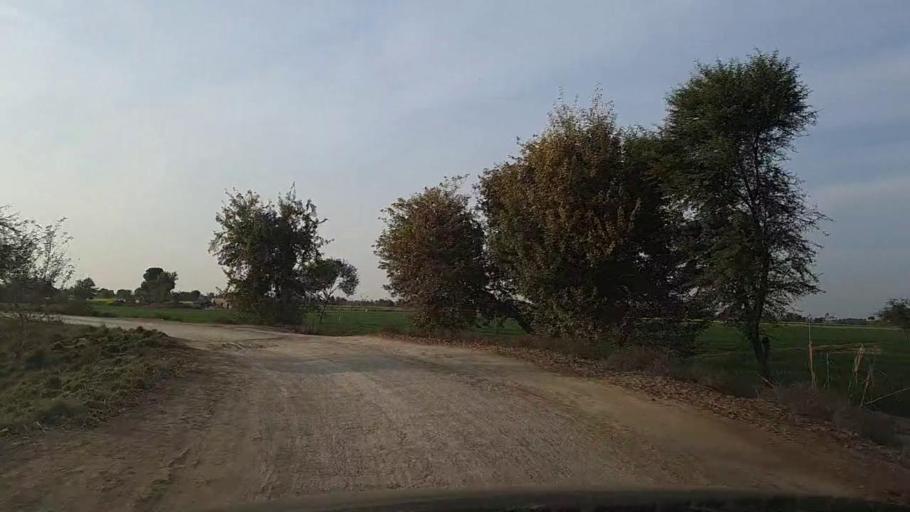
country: PK
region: Sindh
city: Jam Sahib
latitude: 26.4348
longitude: 68.5637
